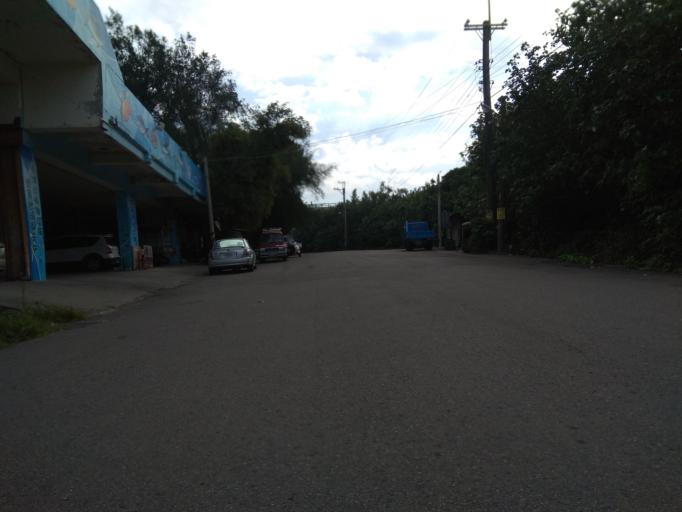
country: TW
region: Taiwan
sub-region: Hsinchu
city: Zhubei
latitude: 24.9259
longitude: 120.9742
